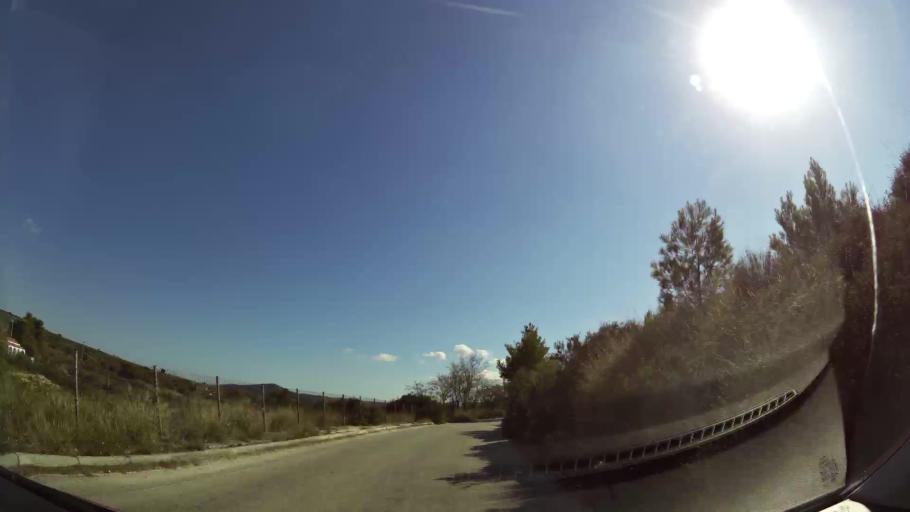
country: GR
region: Attica
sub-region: Nomarchia Anatolikis Attikis
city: Dioni
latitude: 38.0145
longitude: 23.9318
